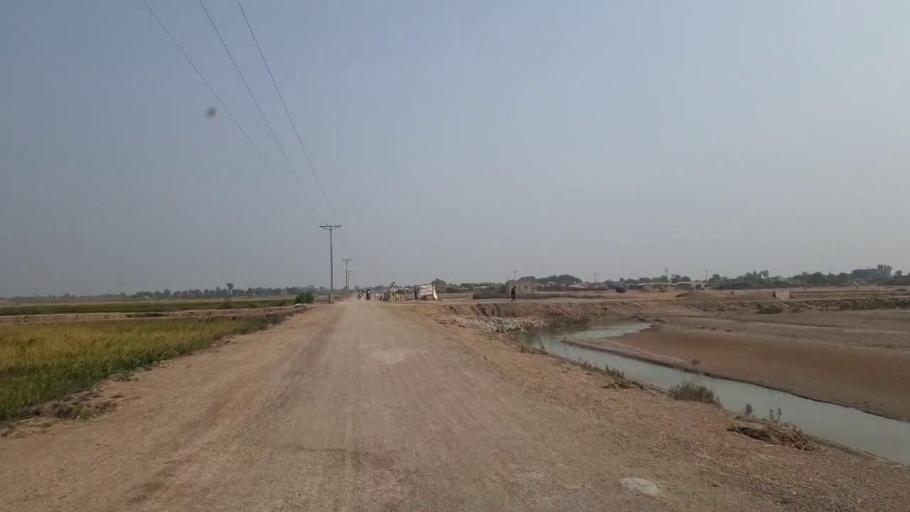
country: PK
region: Sindh
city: Kario
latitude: 24.9082
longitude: 68.5908
